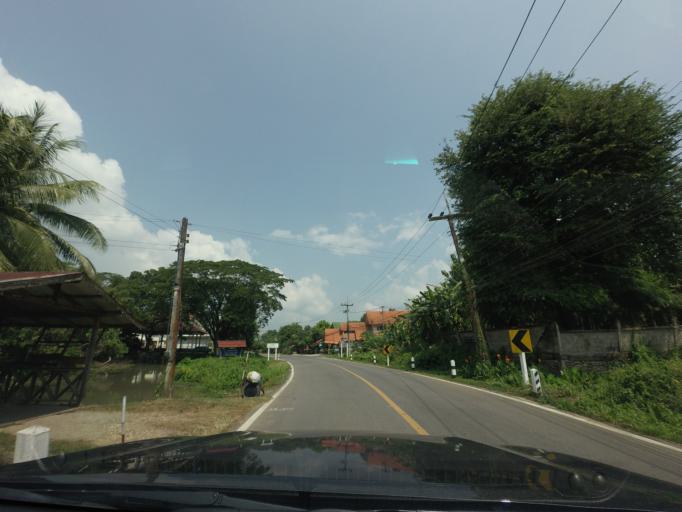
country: TH
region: Nan
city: Santi Suk
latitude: 18.9507
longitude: 100.9231
